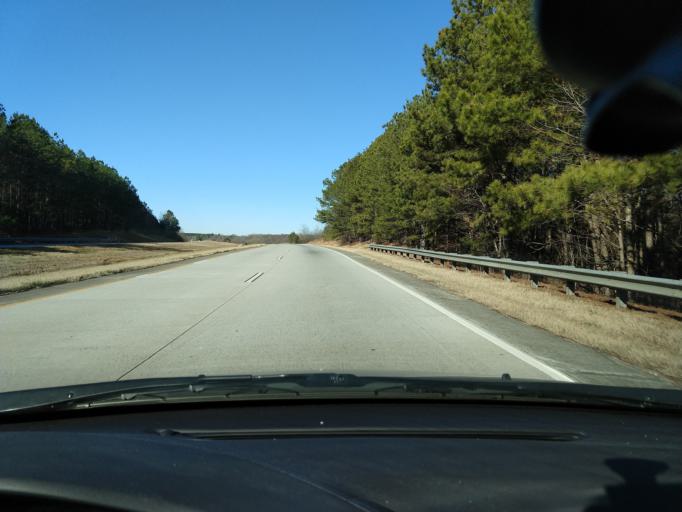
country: US
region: Georgia
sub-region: Barrow County
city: Statham
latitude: 33.9605
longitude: -83.6200
